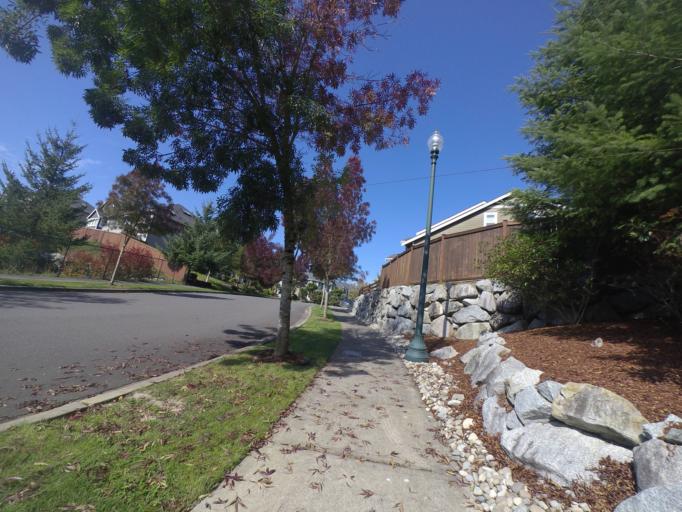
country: US
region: Washington
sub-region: Pierce County
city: Fircrest
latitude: 47.2113
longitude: -122.5286
